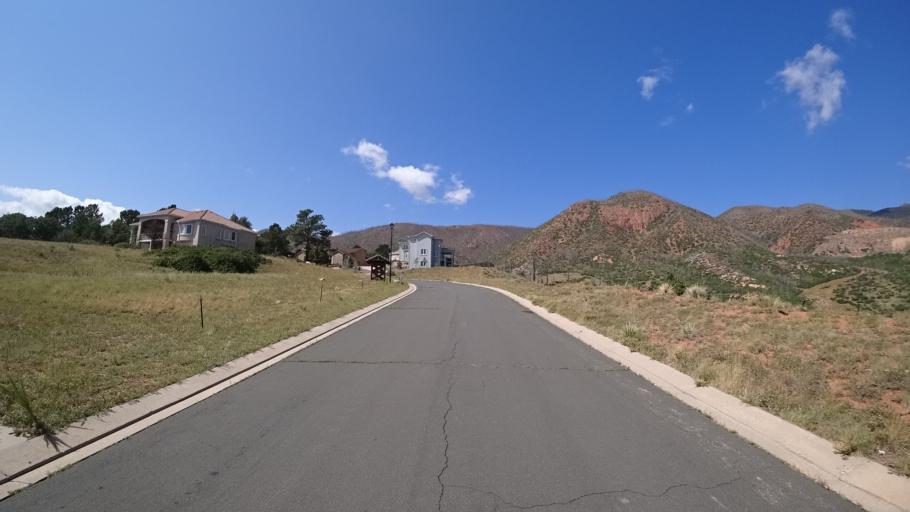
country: US
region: Colorado
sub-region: El Paso County
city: Air Force Academy
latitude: 38.9234
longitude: -104.8811
